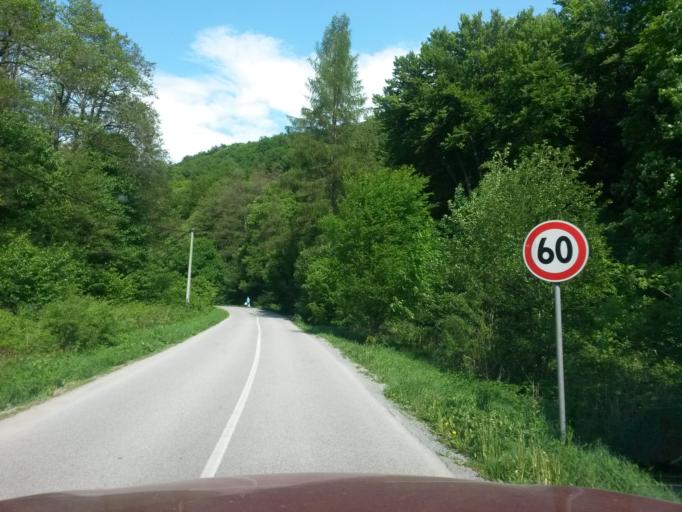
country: SK
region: Kosicky
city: Moldava nad Bodvou
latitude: 48.7267
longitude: 21.0673
